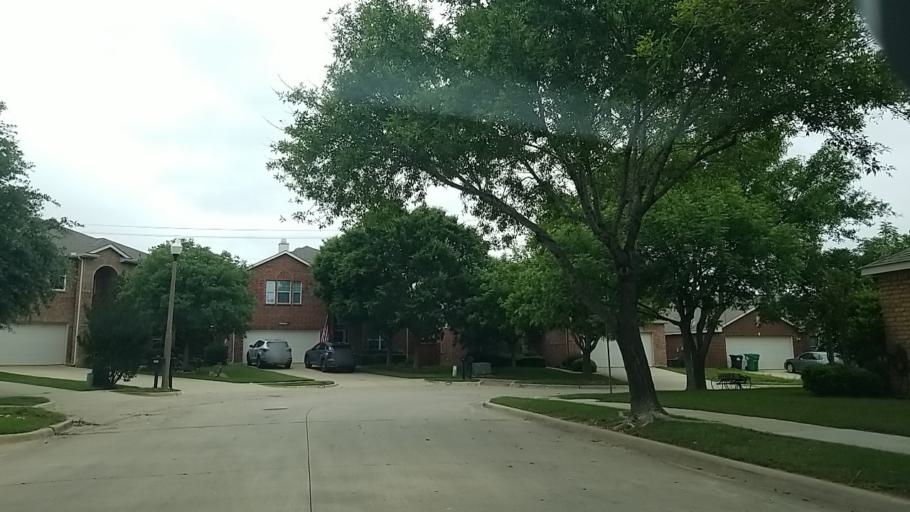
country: US
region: Texas
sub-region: Denton County
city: Corinth
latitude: 33.1702
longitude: -97.0764
